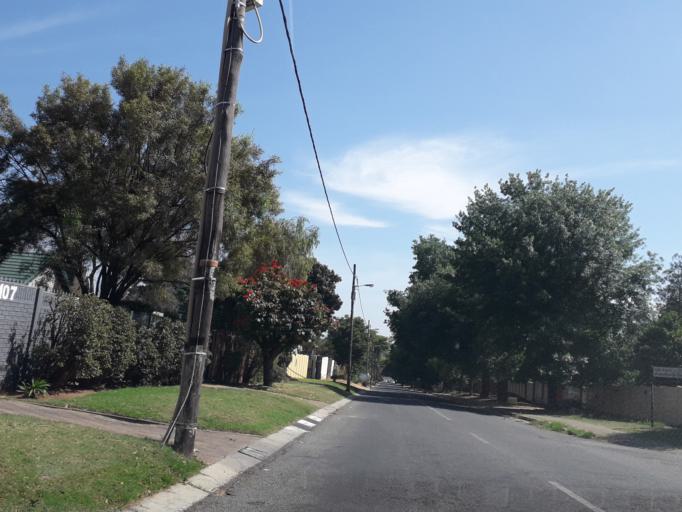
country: ZA
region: Gauteng
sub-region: City of Johannesburg Metropolitan Municipality
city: Johannesburg
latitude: -26.1124
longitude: 28.0020
